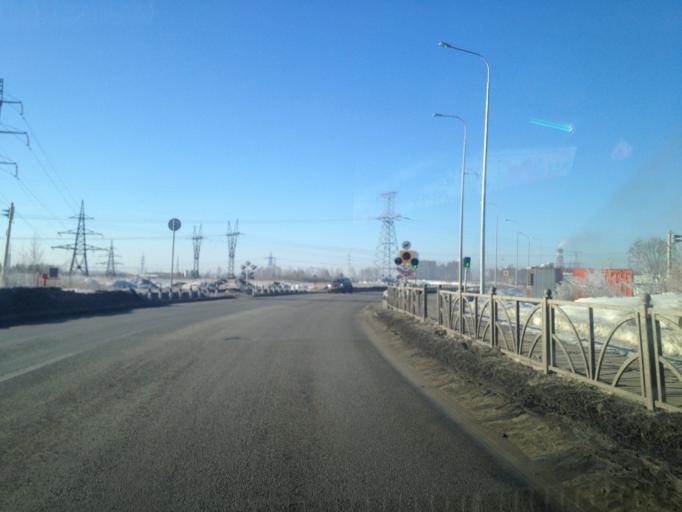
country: RU
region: Sverdlovsk
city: Sovkhoznyy
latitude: 56.7540
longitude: 60.5849
